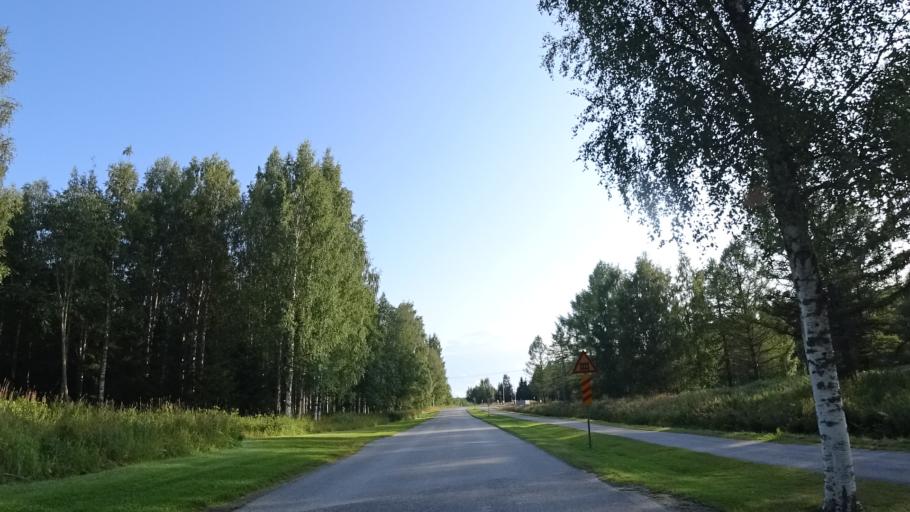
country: FI
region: North Karelia
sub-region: Pielisen Karjala
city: Lieksa
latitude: 63.3120
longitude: 30.0261
